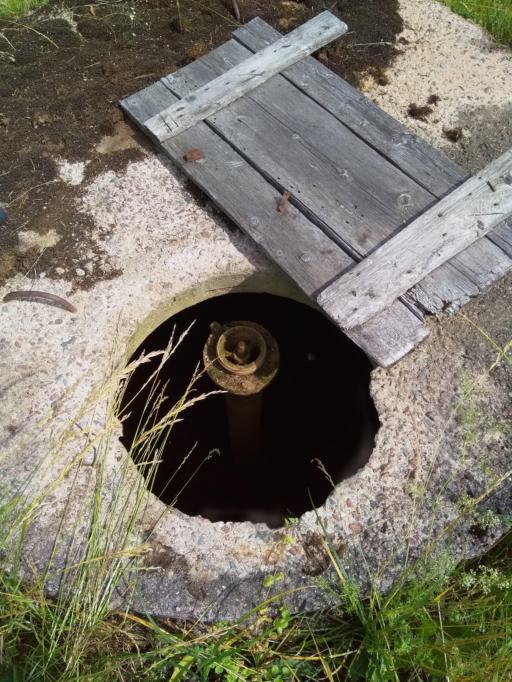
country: BY
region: Mogilev
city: Dashkawka
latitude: 53.7325
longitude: 30.2705
